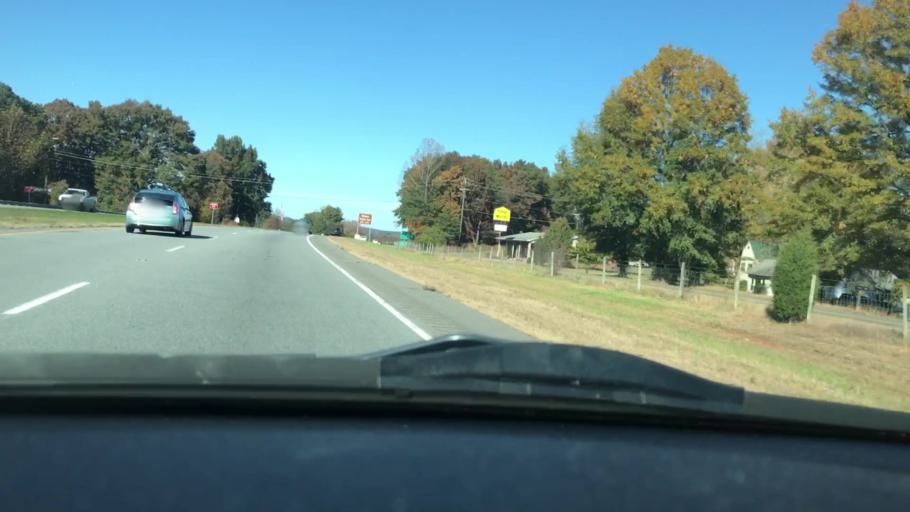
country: US
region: North Carolina
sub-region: Rockingham County
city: Madison
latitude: 36.3691
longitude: -79.9440
